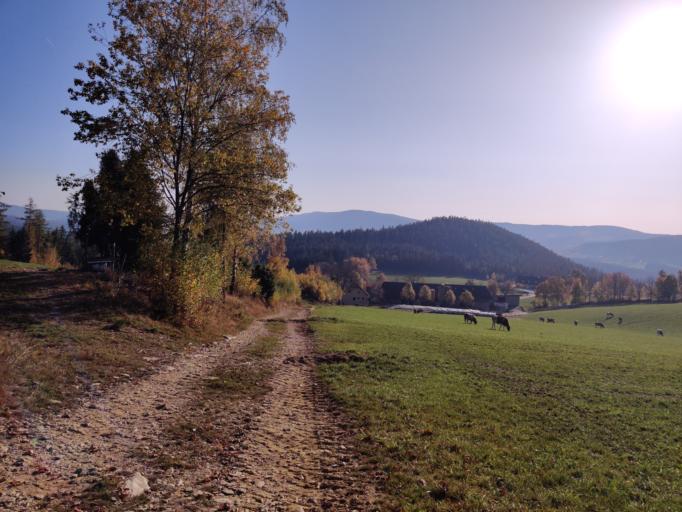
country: AT
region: Styria
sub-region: Politischer Bezirk Hartberg-Fuerstenfeld
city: Sankt Jakob im Walde
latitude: 47.4681
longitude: 15.8103
